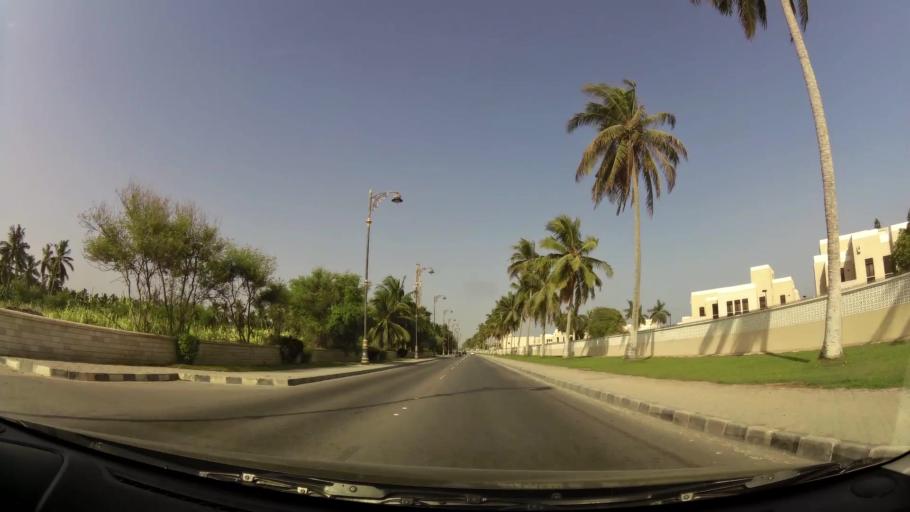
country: OM
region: Zufar
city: Salalah
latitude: 16.9996
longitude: 54.0843
